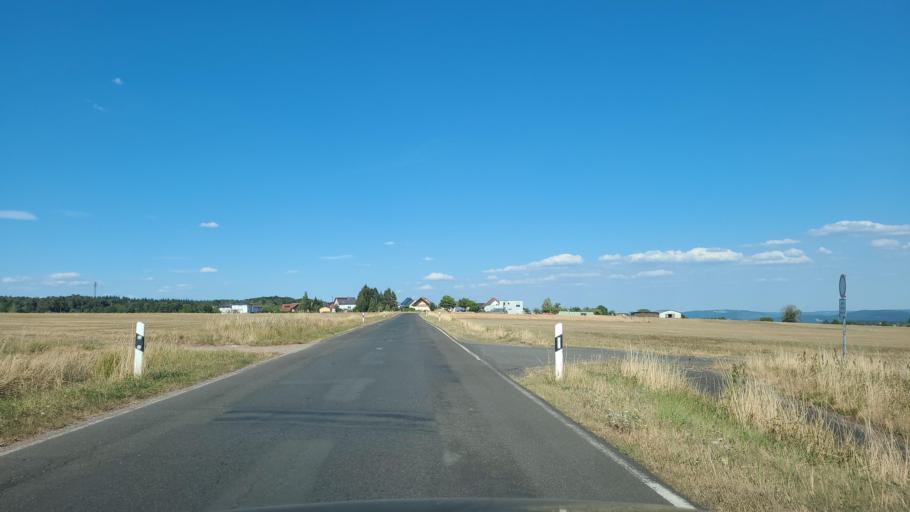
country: DE
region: Rheinland-Pfalz
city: Bergweiler
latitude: 49.9670
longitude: 6.8115
